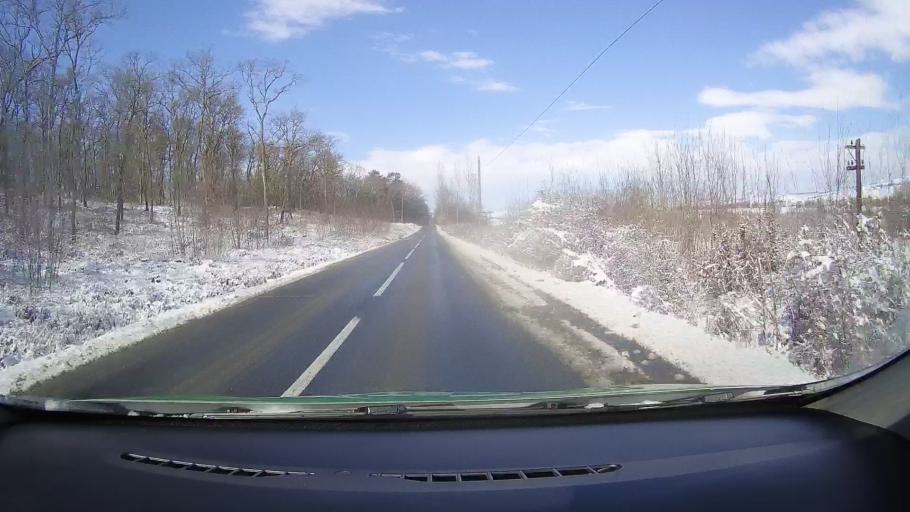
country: RO
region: Sibiu
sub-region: Comuna Nocrich
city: Nocrich
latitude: 45.8662
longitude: 24.4540
